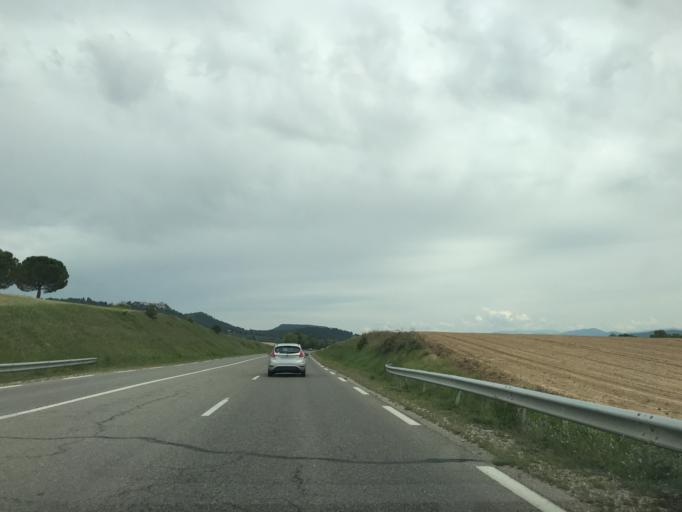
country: FR
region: Provence-Alpes-Cote d'Azur
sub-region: Departement des Alpes-de-Haute-Provence
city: Oraison
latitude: 43.9486
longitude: 5.8895
